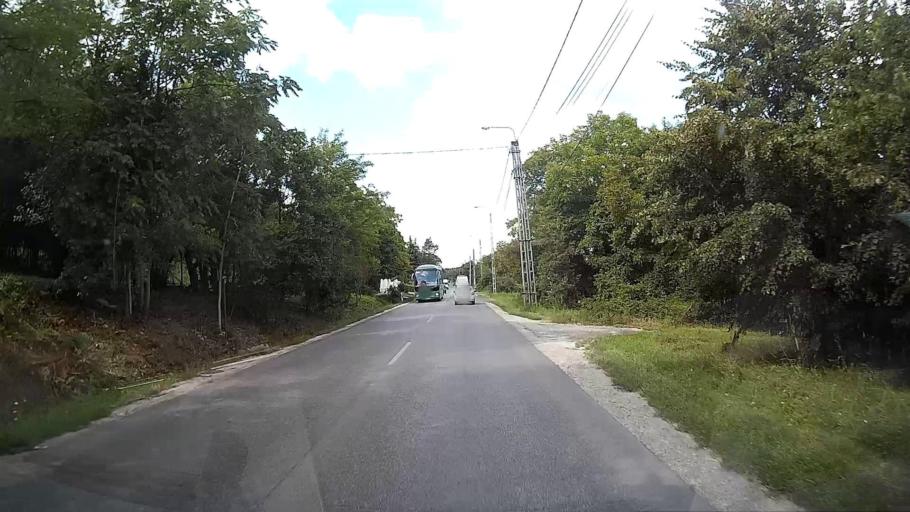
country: HU
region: Pest
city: Leanyfalu
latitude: 47.7324
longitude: 19.0885
